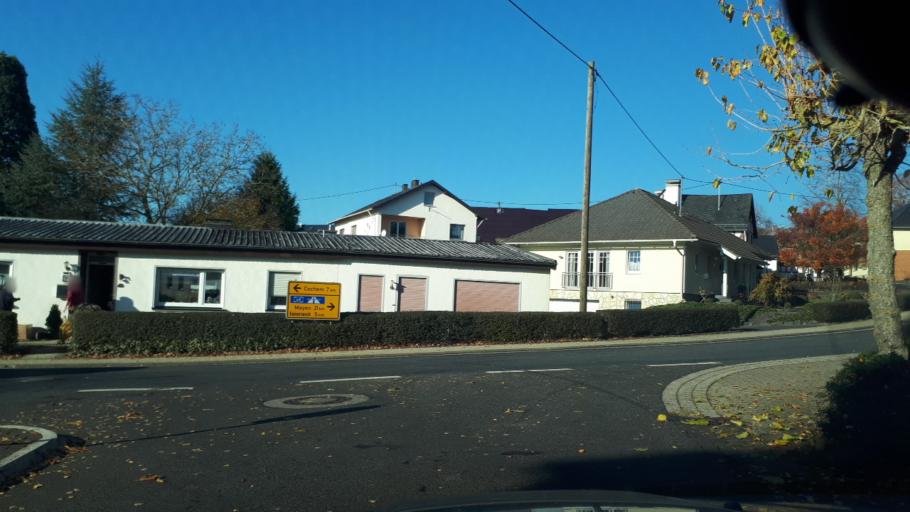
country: DE
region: Rheinland-Pfalz
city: Landkern
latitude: 50.1947
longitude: 7.1540
